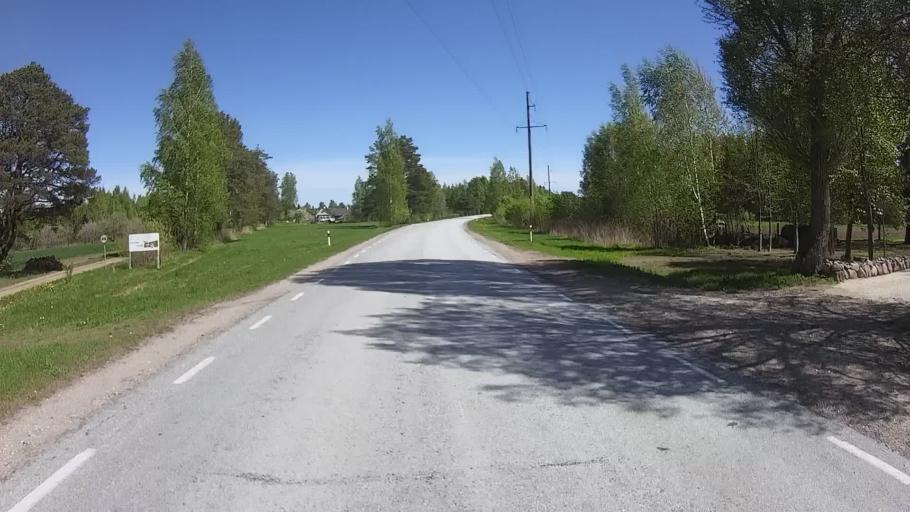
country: EE
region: Polvamaa
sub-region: Raepina vald
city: Rapina
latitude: 58.0862
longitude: 27.4392
